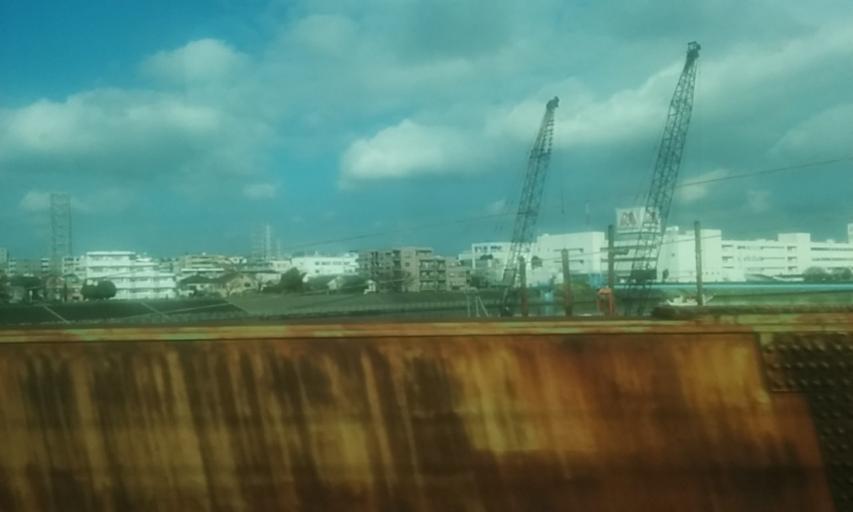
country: JP
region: Kanagawa
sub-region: Kawasaki-shi
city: Kawasaki
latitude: 35.5156
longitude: 139.6785
